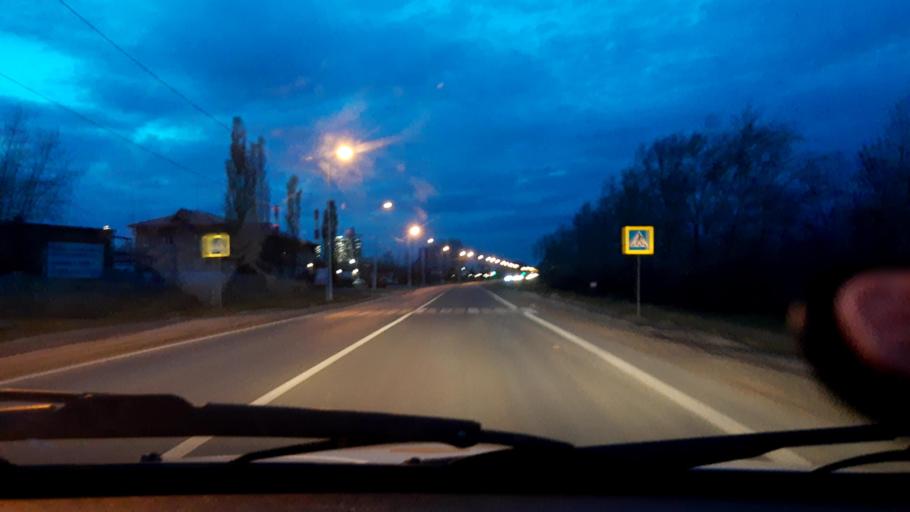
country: RU
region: Bashkortostan
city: Ufa
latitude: 54.8460
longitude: 56.1201
